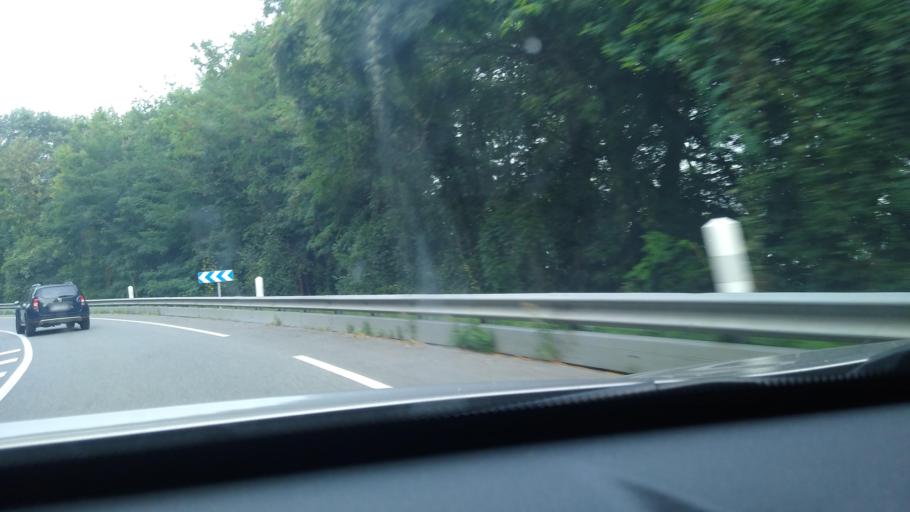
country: FR
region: Midi-Pyrenees
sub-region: Departement de la Haute-Garonne
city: Salies-du-Salat
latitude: 43.1197
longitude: 0.9323
